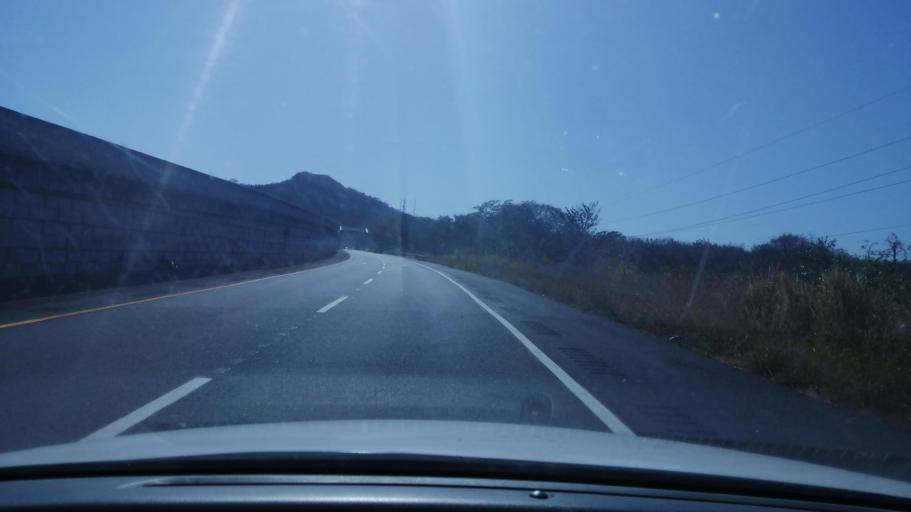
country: PA
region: Chiriqui
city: San Felix
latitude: 8.2805
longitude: -82.0483
